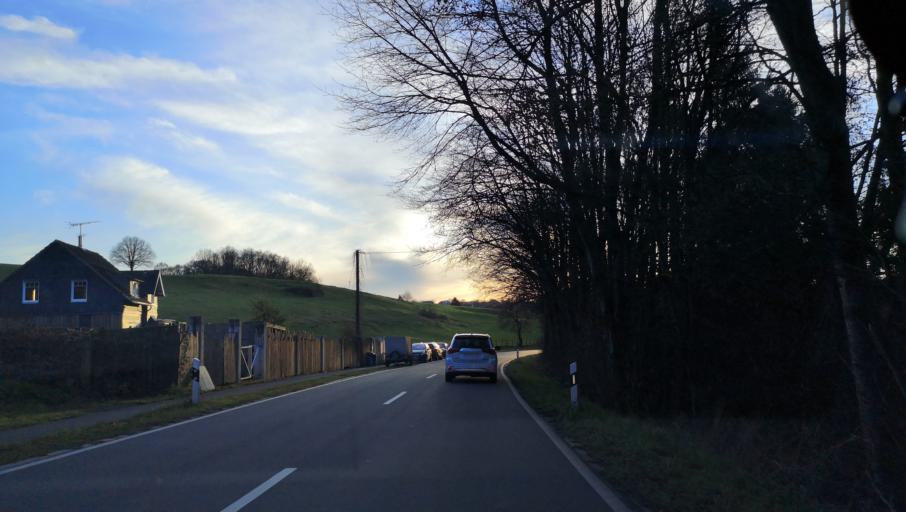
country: DE
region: North Rhine-Westphalia
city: Huckeswagen
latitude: 51.1541
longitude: 7.3523
